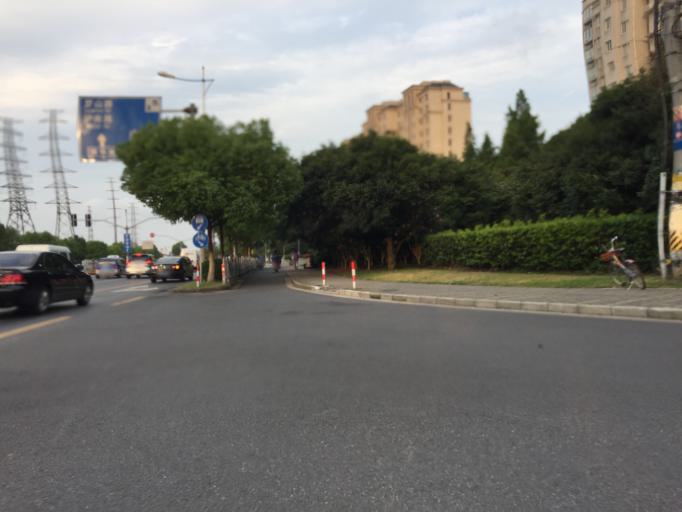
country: CN
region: Shanghai Shi
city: Huamu
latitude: 31.1895
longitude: 121.5405
